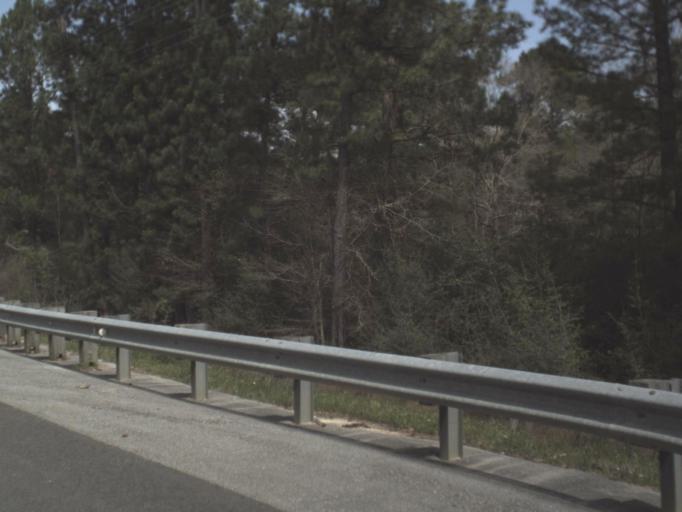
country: US
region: Alabama
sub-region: Geneva County
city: Geneva
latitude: 30.8989
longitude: -85.9547
